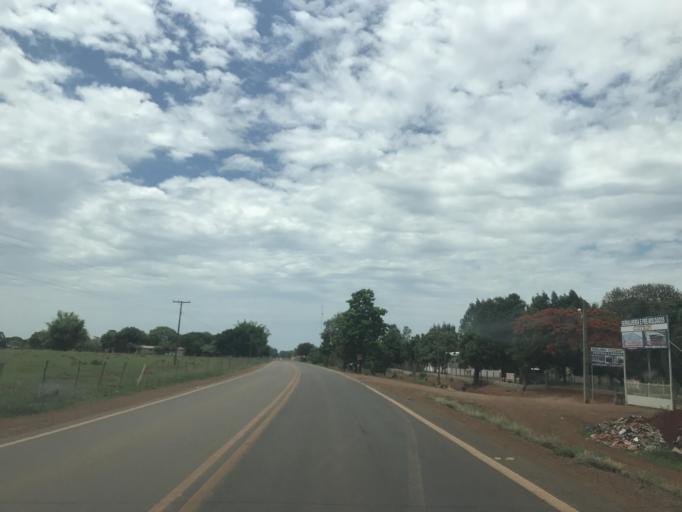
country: BR
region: Goias
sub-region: Luziania
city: Luziania
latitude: -16.3258
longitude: -48.0196
